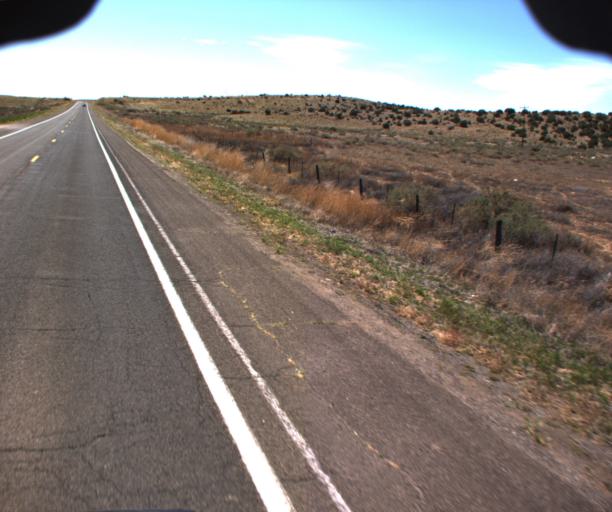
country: US
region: Arizona
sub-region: Mohave County
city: Peach Springs
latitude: 35.5247
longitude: -113.4414
